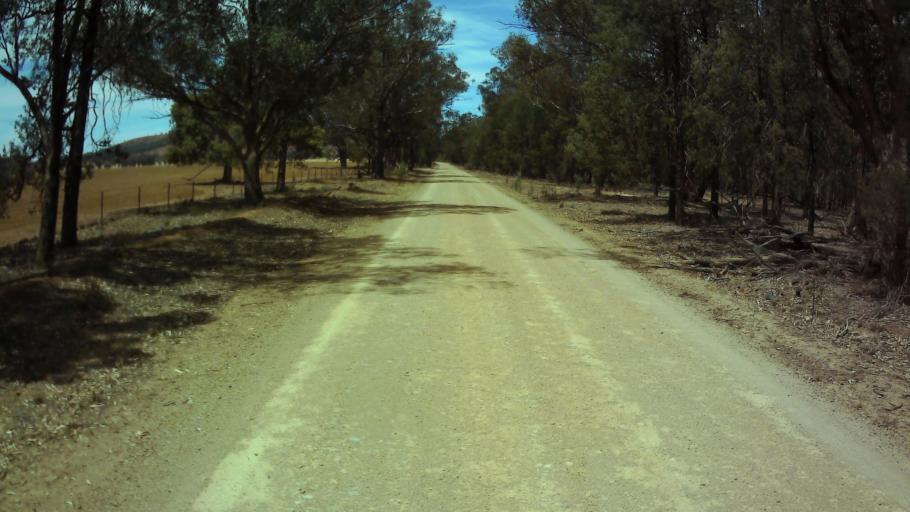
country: AU
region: New South Wales
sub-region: Weddin
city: Grenfell
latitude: -33.7617
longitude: 148.1246
